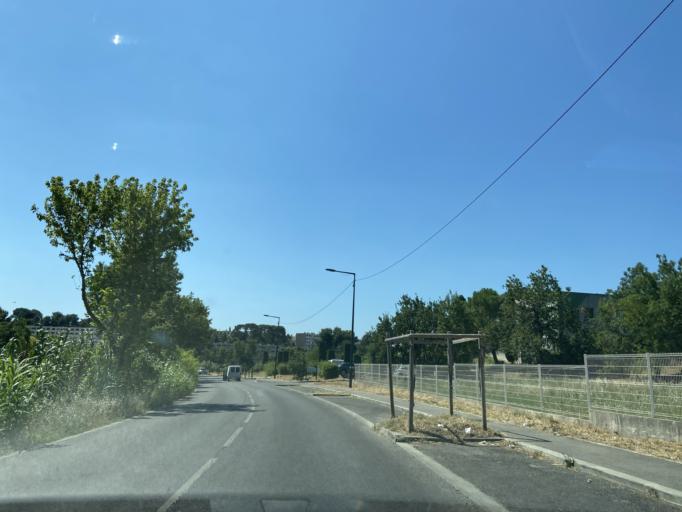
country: FR
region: Provence-Alpes-Cote d'Azur
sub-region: Departement des Bouches-du-Rhone
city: Plan-de-Cuques
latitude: 43.3409
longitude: 5.4365
